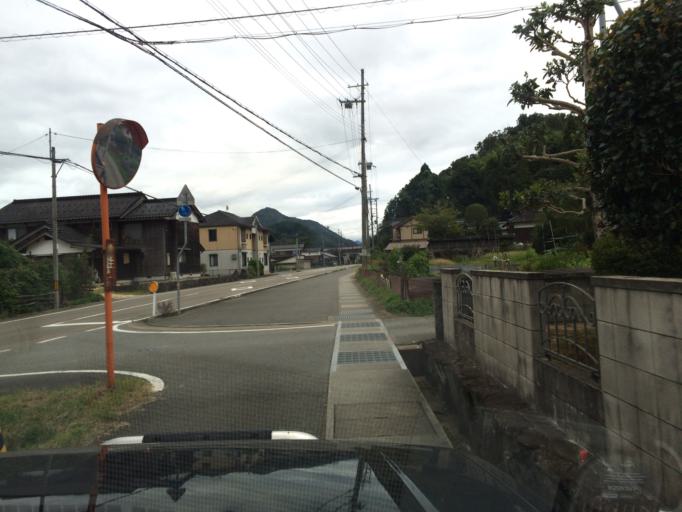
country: JP
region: Hyogo
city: Toyooka
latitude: 35.4782
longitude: 134.7763
